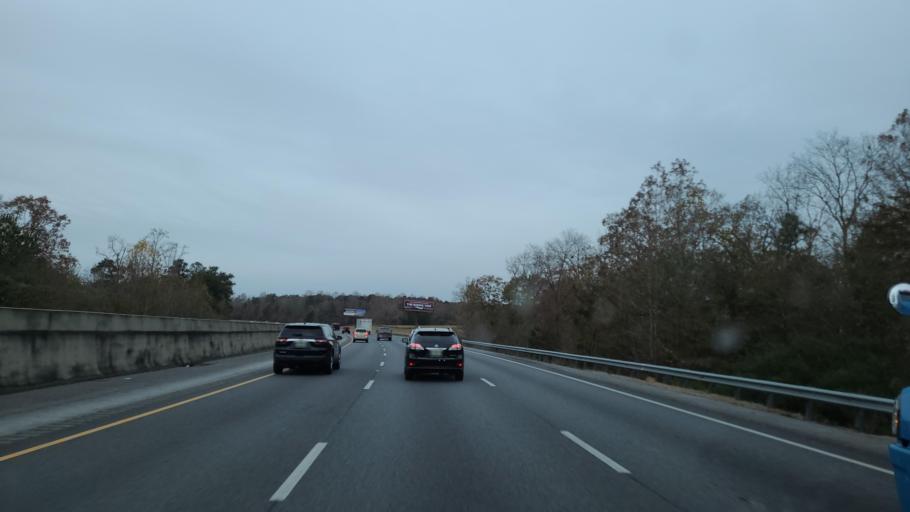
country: US
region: Alabama
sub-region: Tuscaloosa County
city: Vance
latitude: 33.2109
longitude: -87.2178
